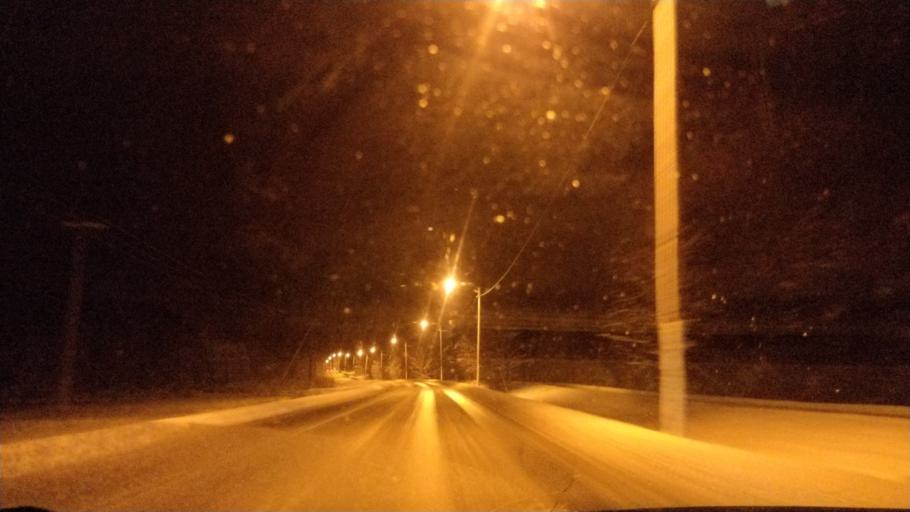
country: FI
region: Lapland
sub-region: Rovaniemi
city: Rovaniemi
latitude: 66.3026
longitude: 25.3550
